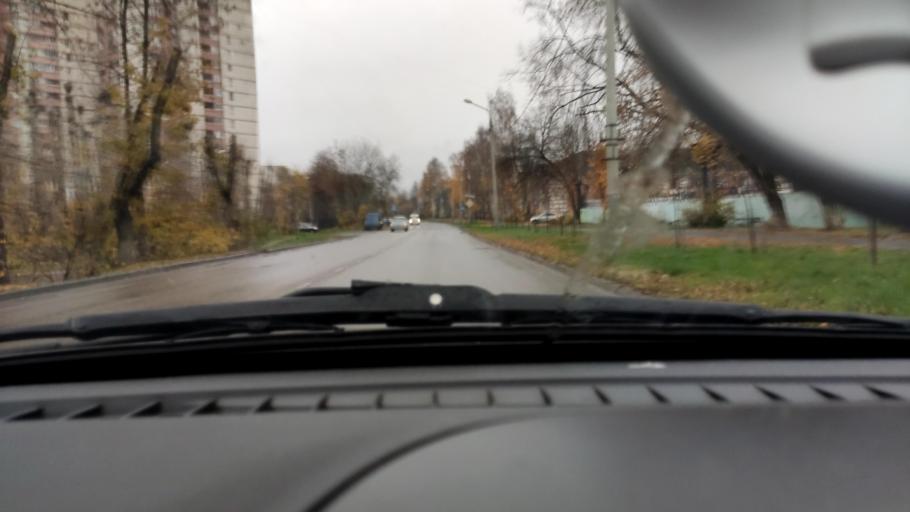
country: RU
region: Perm
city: Kultayevo
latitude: 57.9972
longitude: 55.9499
